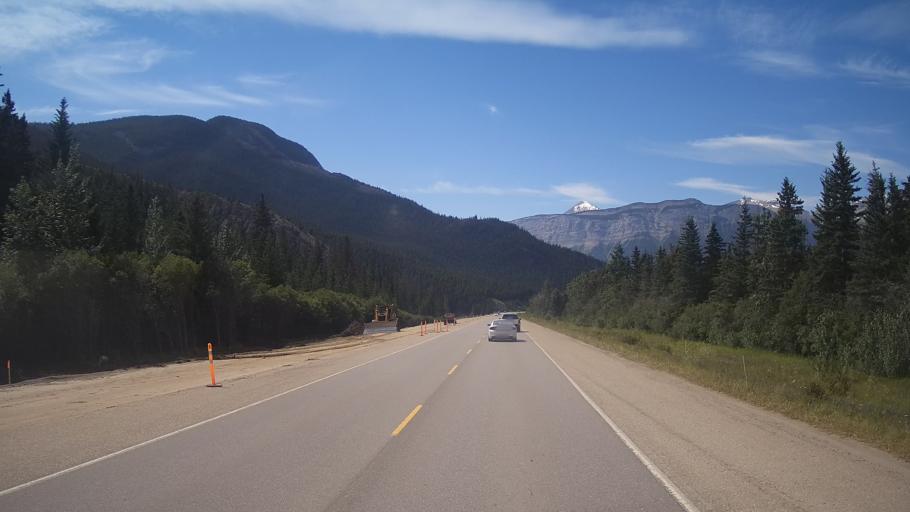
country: CA
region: Alberta
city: Jasper Park Lodge
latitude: 53.0597
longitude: -118.0673
